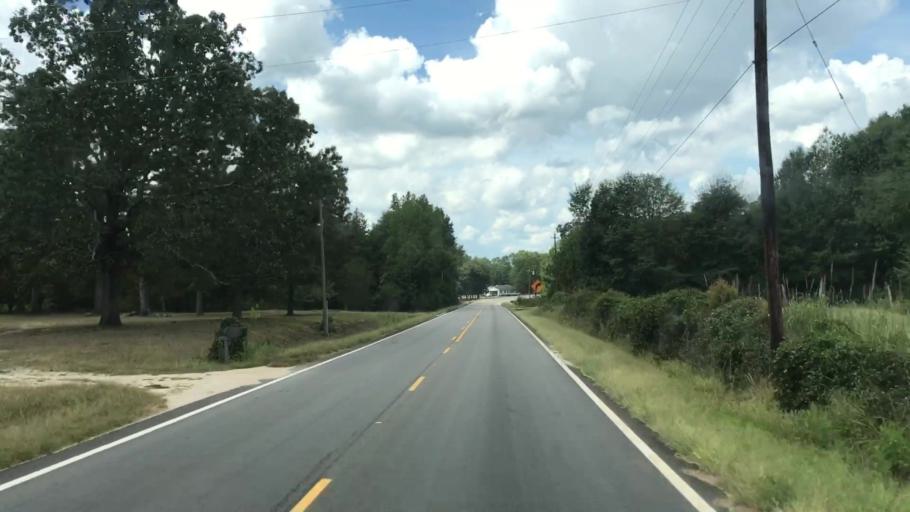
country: US
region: Georgia
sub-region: Greene County
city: Greensboro
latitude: 33.5594
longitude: -83.1283
